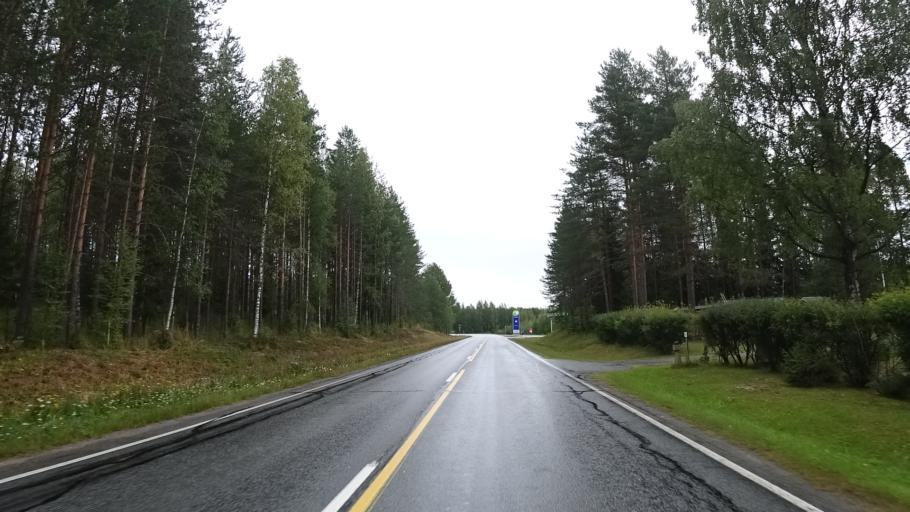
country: FI
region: North Karelia
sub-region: Keski-Karjala
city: Raeaekkylae
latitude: 62.0540
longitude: 29.6102
